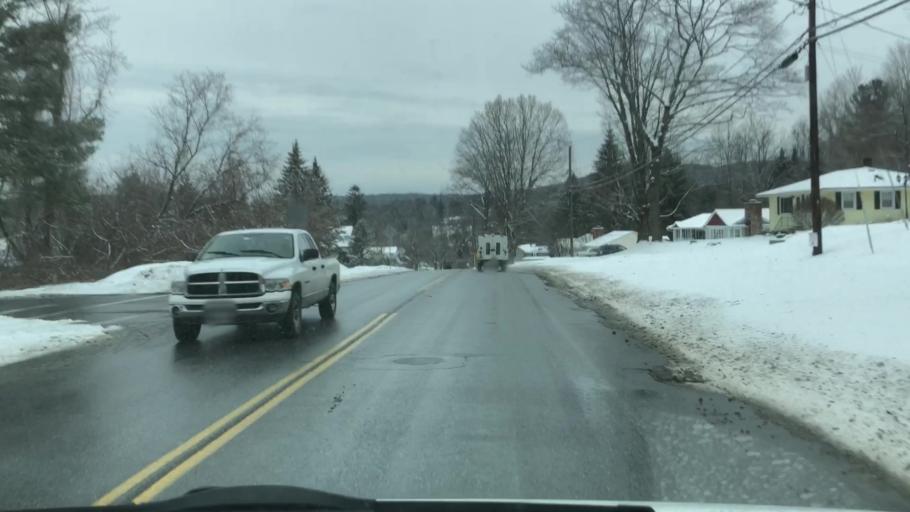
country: US
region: Massachusetts
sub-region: Berkshire County
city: Dalton
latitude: 42.4653
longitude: -73.1815
